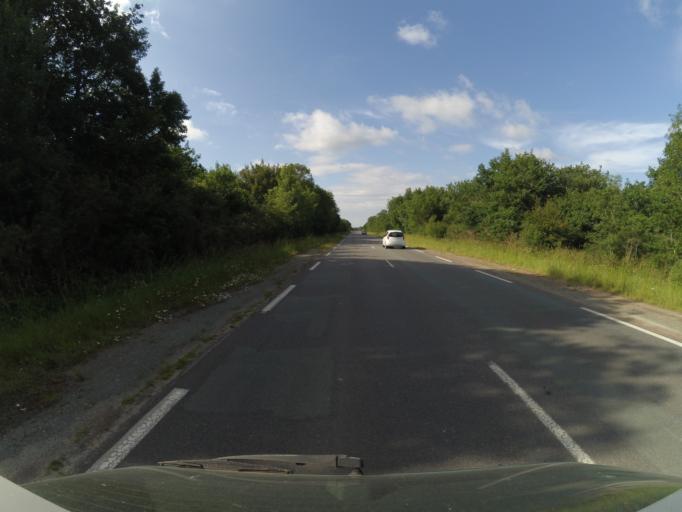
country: FR
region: Poitou-Charentes
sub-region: Departement de la Charente-Maritime
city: Le Gua
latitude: 45.7890
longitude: -0.9362
